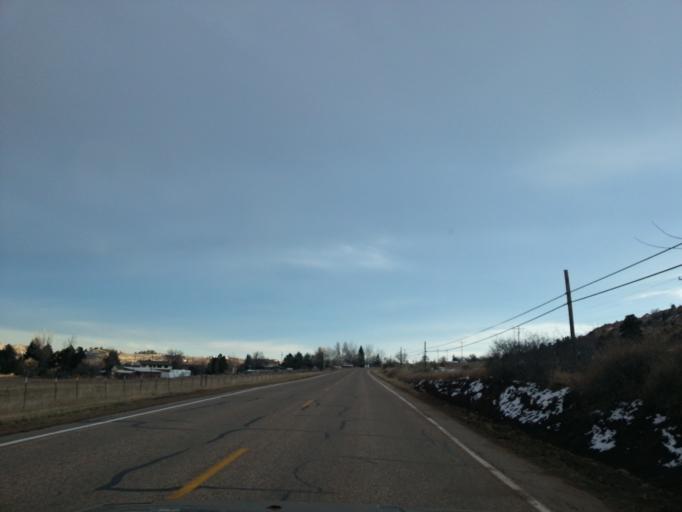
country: US
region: Colorado
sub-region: Larimer County
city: Loveland
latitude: 40.4415
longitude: -105.1998
